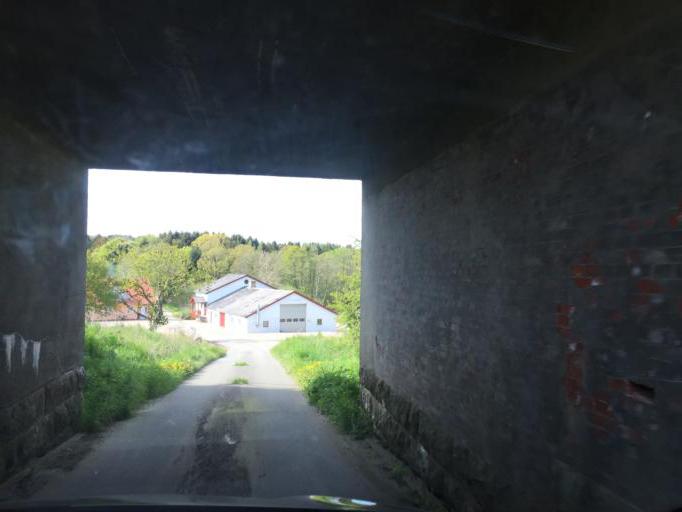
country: DK
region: South Denmark
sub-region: Fredericia Kommune
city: Taulov
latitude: 55.5332
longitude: 9.5653
